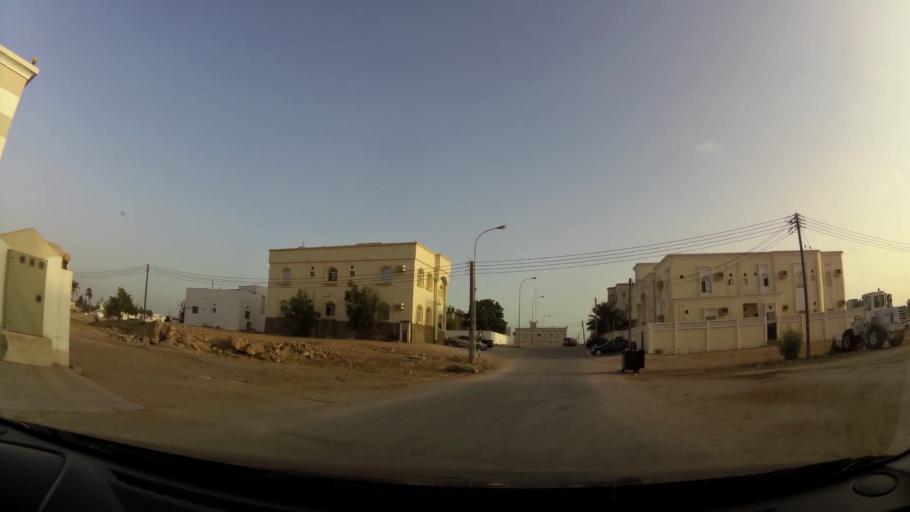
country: OM
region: Zufar
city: Salalah
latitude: 17.0015
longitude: 54.0343
